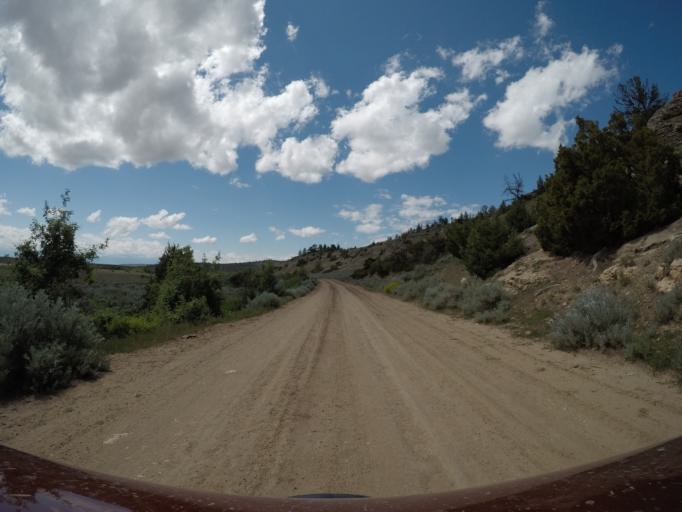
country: US
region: Montana
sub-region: Yellowstone County
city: Laurel
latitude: 45.2436
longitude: -108.6490
